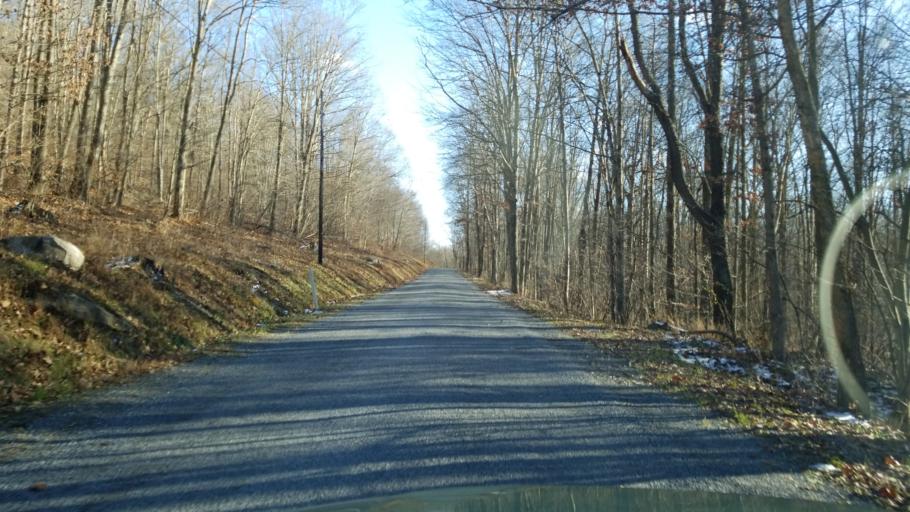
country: US
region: Pennsylvania
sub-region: Jefferson County
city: Brockway
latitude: 41.2750
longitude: -78.8150
